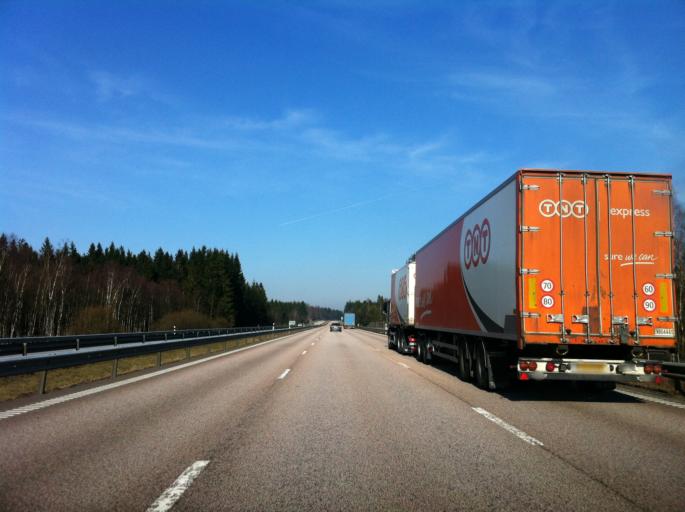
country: SE
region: Skane
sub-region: Bastads Kommun
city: Bastad
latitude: 56.3615
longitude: 12.9354
